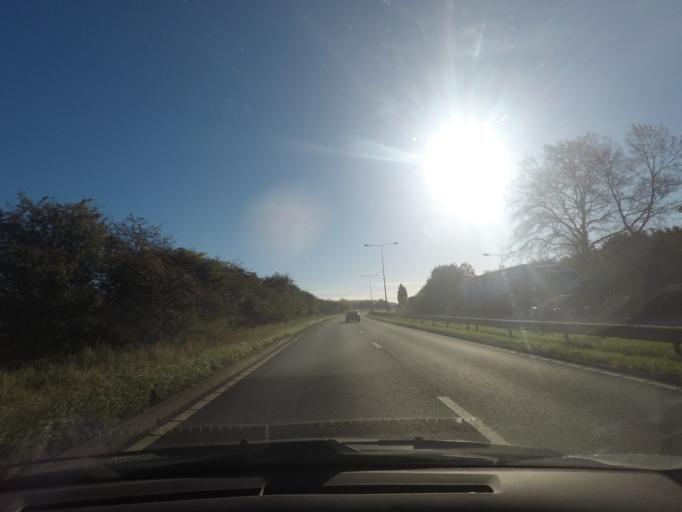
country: GB
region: England
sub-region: East Riding of Yorkshire
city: South Cave
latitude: 53.7602
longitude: -0.5928
